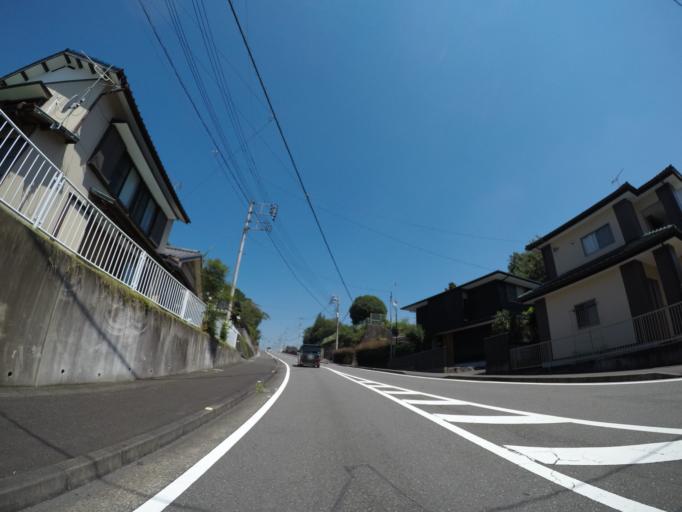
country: JP
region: Shizuoka
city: Fujinomiya
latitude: 35.2047
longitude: 138.5659
